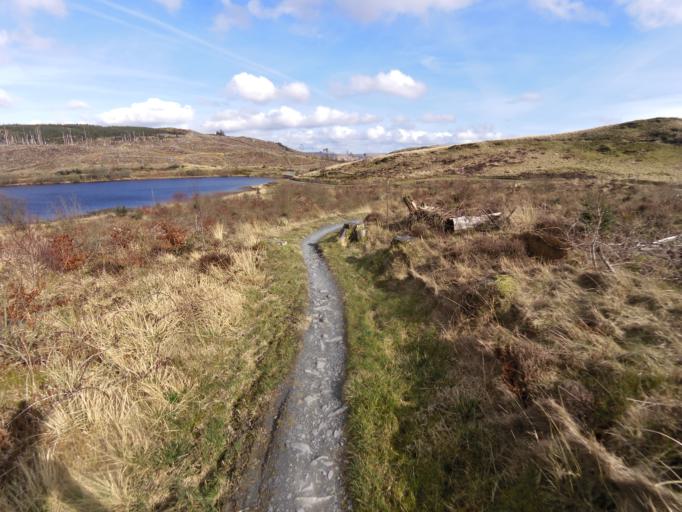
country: GB
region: Wales
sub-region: County of Ceredigion
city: Bow Street
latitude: 52.4340
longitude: -3.8934
